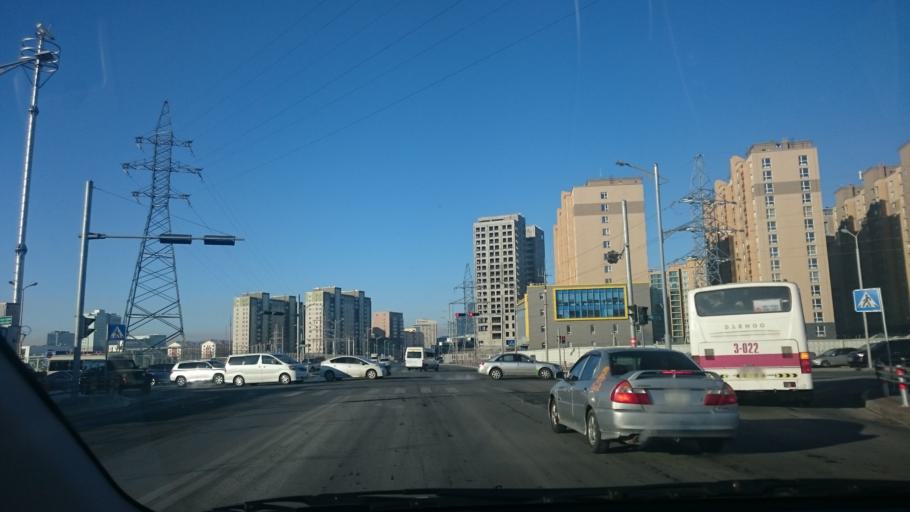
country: MN
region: Ulaanbaatar
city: Ulaanbaatar
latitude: 47.8994
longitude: 106.9312
